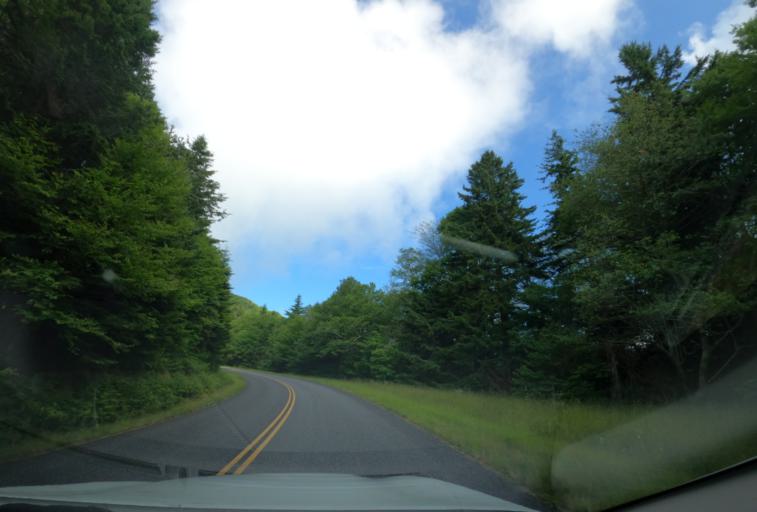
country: US
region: North Carolina
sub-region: Haywood County
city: Hazelwood
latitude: 35.3183
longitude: -82.9593
